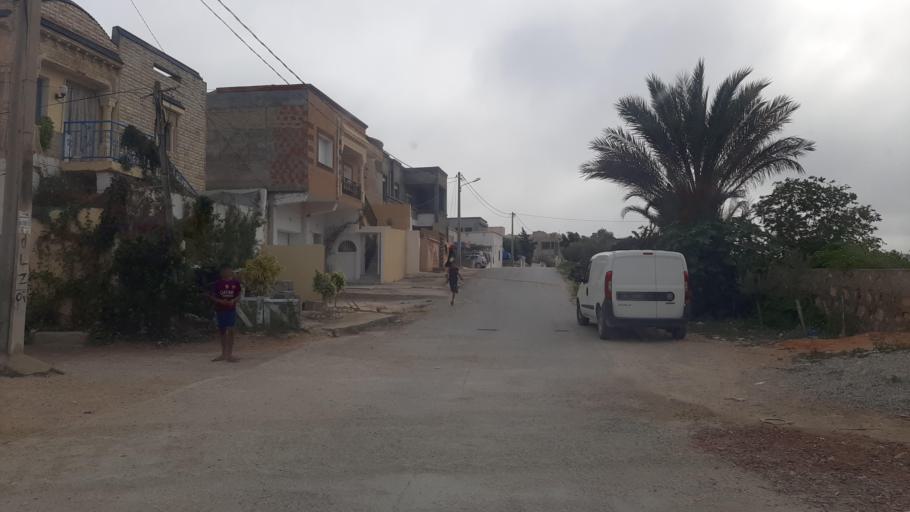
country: TN
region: Nabul
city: Menzel Heurr
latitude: 36.6762
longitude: 10.9224
